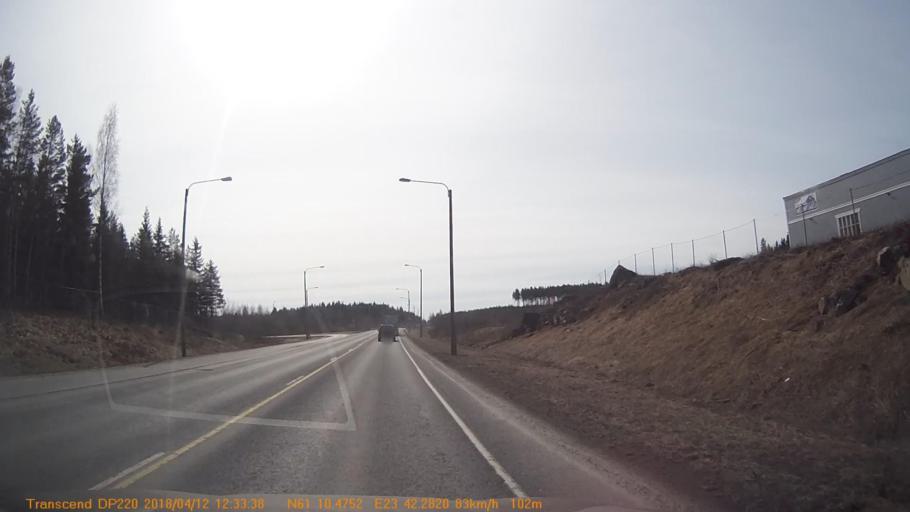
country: FI
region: Pirkanmaa
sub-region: Etelae-Pirkanmaa
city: Kylmaekoski
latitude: 61.1742
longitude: 23.7045
